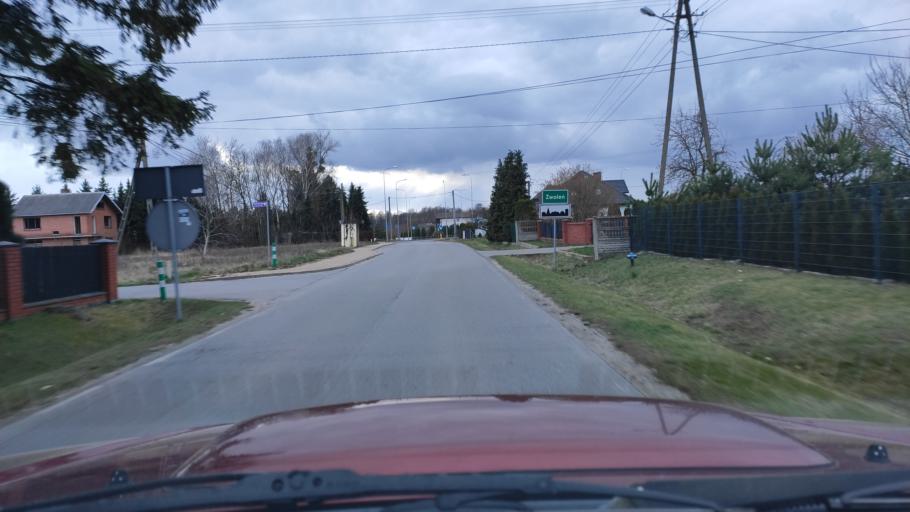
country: PL
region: Masovian Voivodeship
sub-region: Powiat zwolenski
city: Zwolen
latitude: 51.3781
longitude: 21.5969
